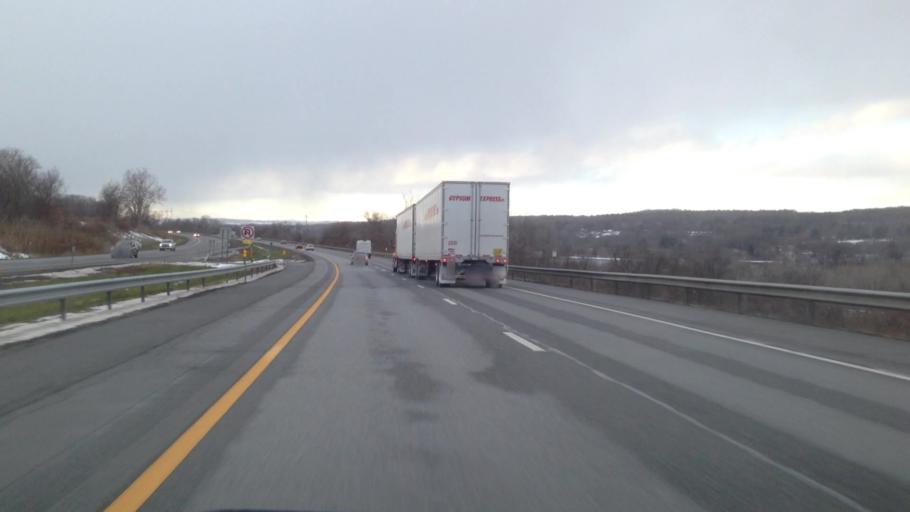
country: US
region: New York
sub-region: Montgomery County
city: Saint Johnsville
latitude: 42.9873
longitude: -74.6666
